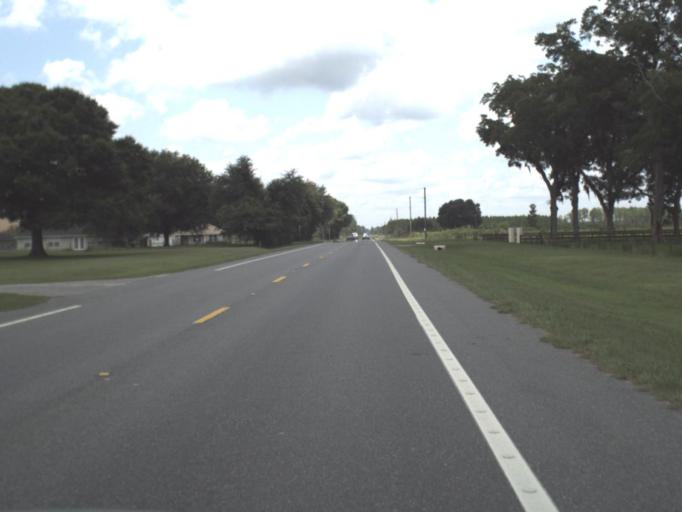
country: US
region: Florida
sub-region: Union County
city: Lake Butler
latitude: 30.0209
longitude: -82.3688
